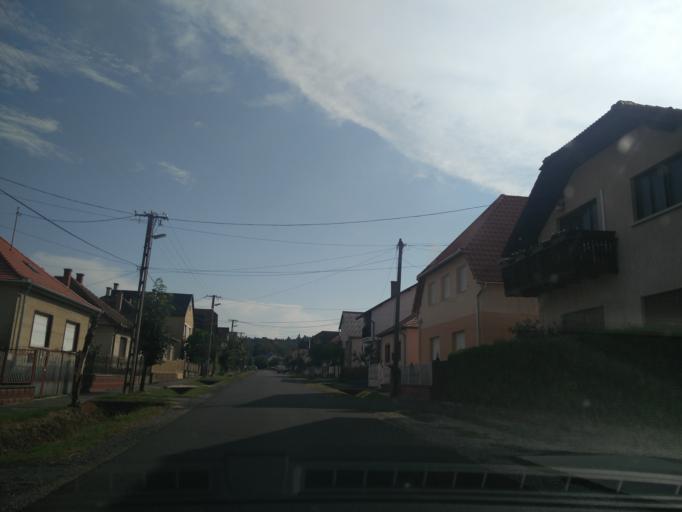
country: HU
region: Zala
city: Zalaegerszeg
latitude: 46.8491
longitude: 16.8190
